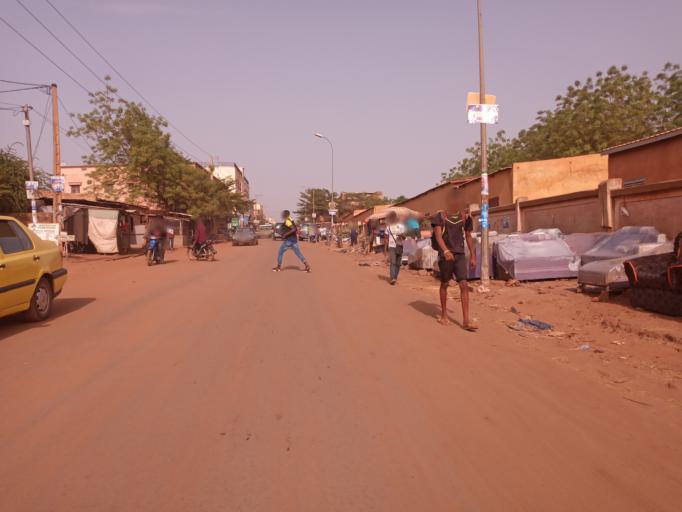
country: ML
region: Bamako
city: Bamako
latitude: 12.6794
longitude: -7.9438
